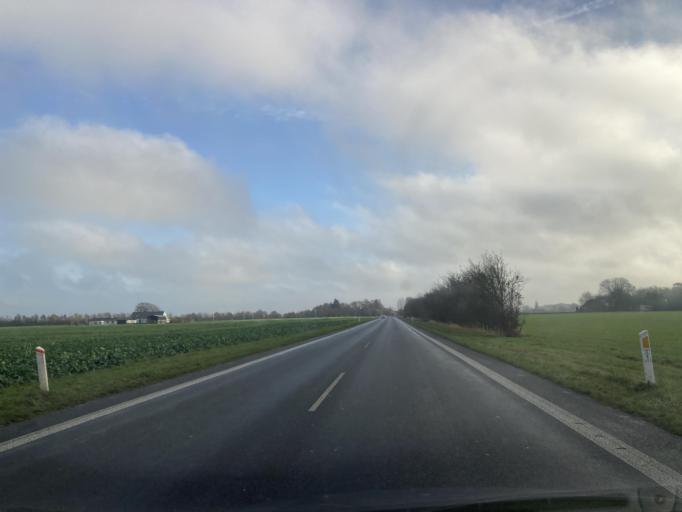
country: DK
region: Zealand
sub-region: Lolland Kommune
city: Maribo
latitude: 54.8138
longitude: 11.3969
